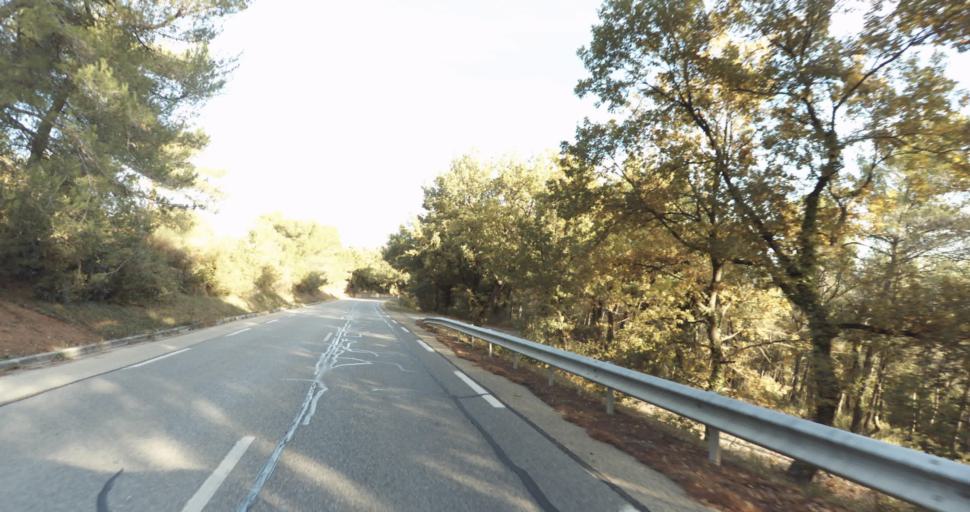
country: FR
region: Provence-Alpes-Cote d'Azur
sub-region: Departement des Bouches-du-Rhone
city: Venelles
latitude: 43.6195
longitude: 5.4622
